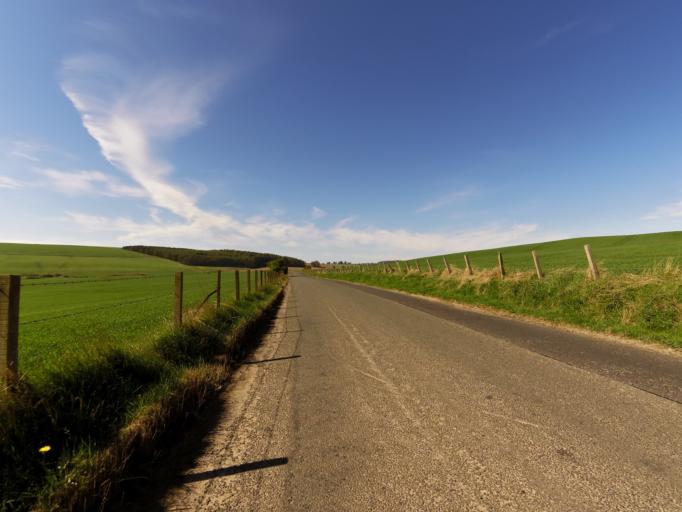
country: GB
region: Scotland
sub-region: Fife
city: Newport-On-Tay
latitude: 56.4135
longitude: -2.9863
